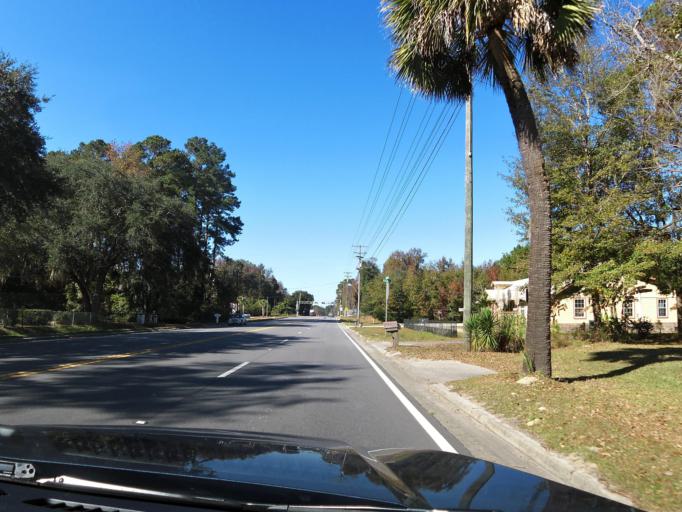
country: US
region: Georgia
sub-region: Liberty County
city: Midway
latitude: 31.7942
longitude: -81.4034
